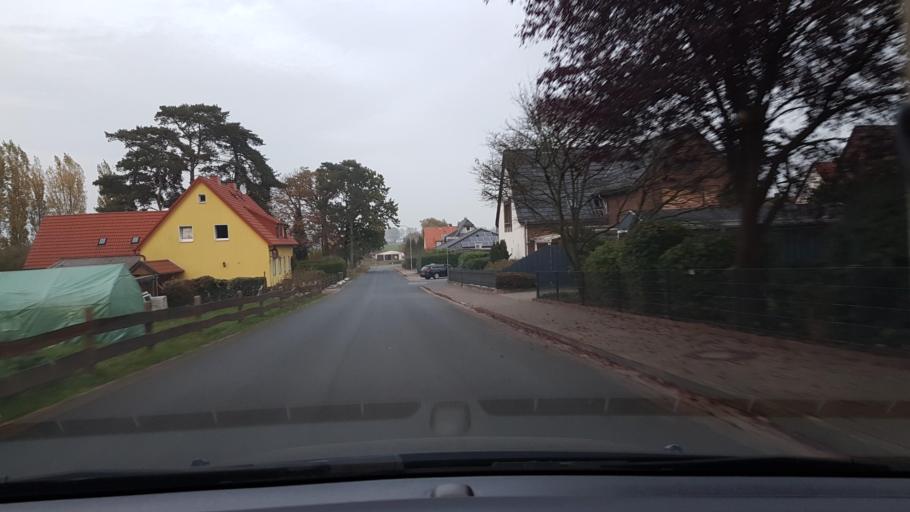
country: DE
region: Lower Saxony
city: Hagenburg
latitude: 52.4367
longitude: 9.3478
